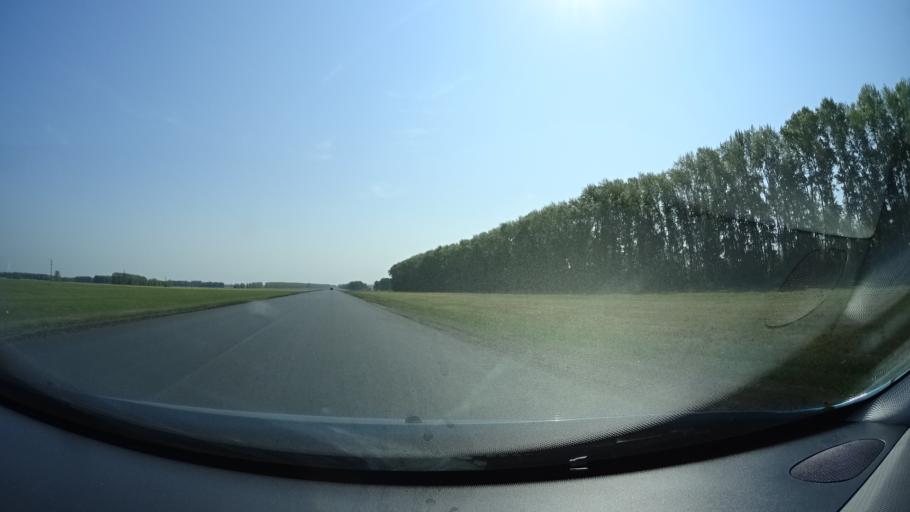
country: RU
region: Bashkortostan
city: Karmaskaly
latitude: 54.4036
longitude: 56.0838
